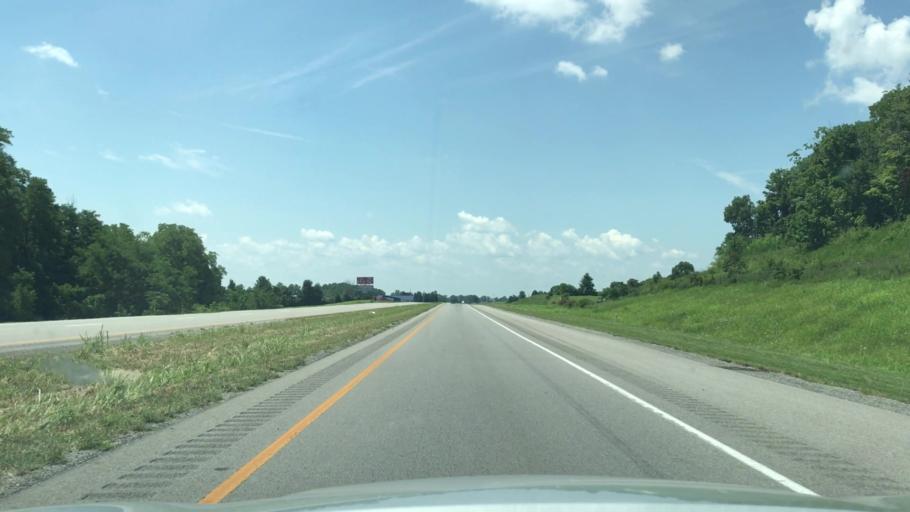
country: US
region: Kentucky
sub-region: Clinton County
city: Albany
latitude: 36.7276
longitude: -85.1360
